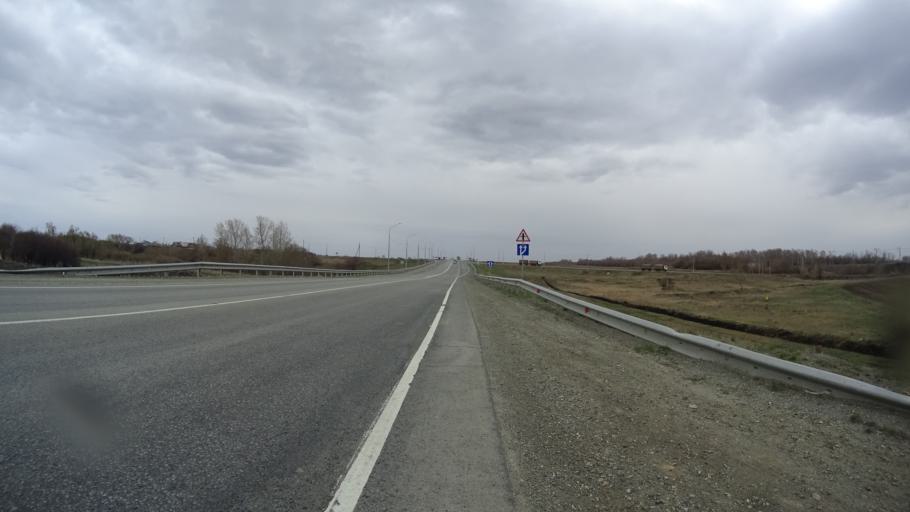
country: RU
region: Chelyabinsk
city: Krasnogorskiy
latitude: 54.6761
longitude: 61.2482
